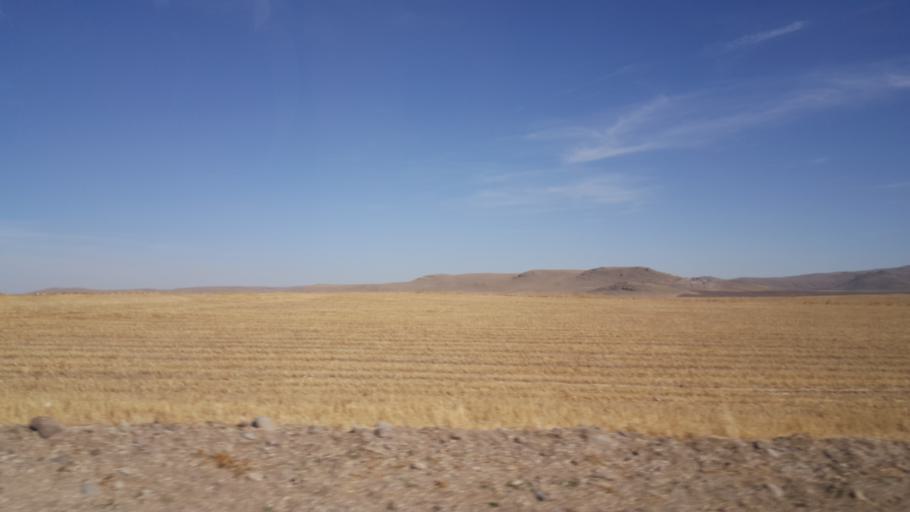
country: TR
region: Ankara
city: Yenice
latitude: 39.3278
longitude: 32.7548
